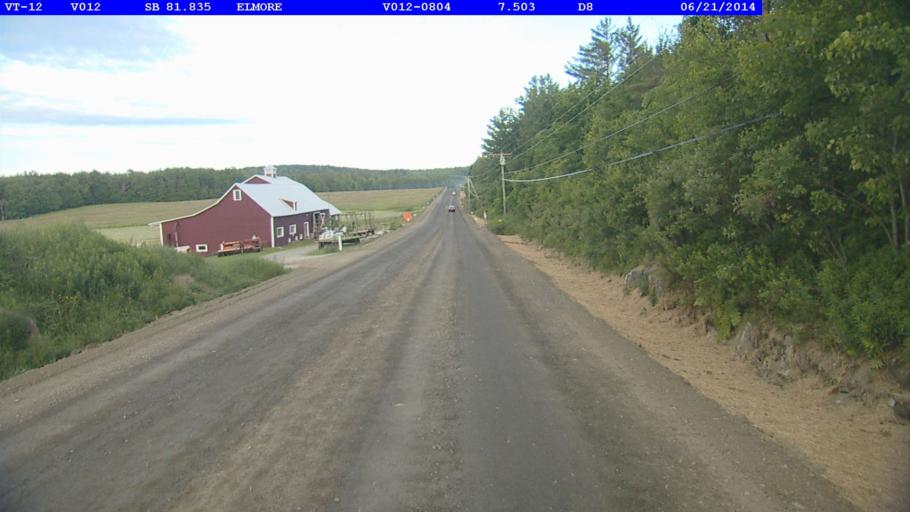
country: US
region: Vermont
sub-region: Lamoille County
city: Morrisville
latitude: 44.5486
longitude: -72.5338
